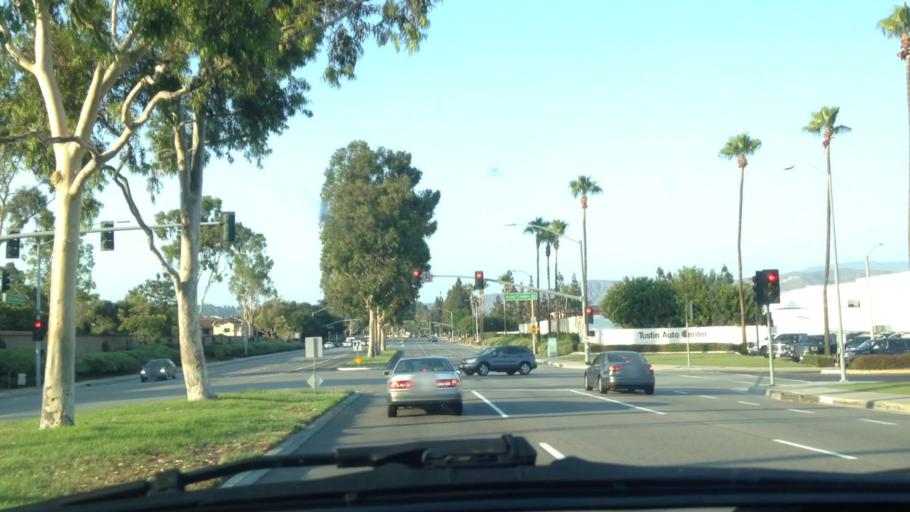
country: US
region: California
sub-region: Orange County
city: Tustin
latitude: 33.7276
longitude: -117.8020
